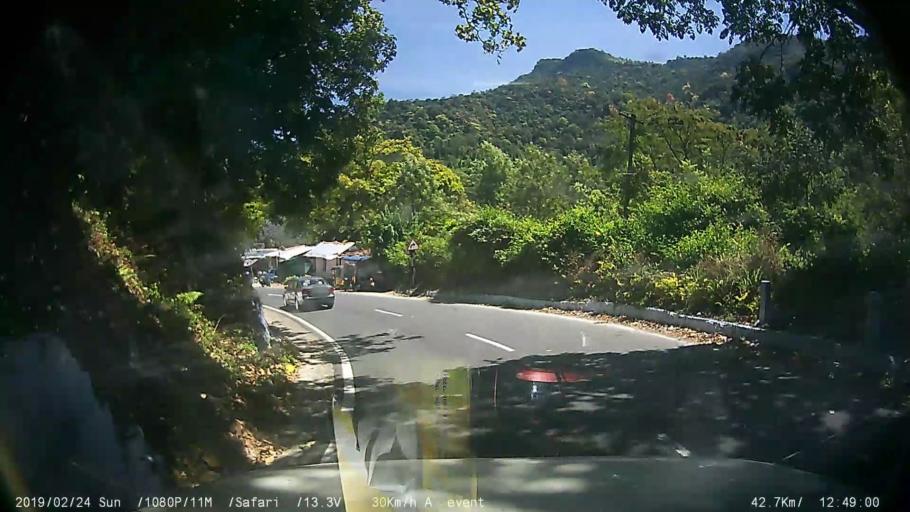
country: IN
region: Tamil Nadu
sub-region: Nilgiri
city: Wellington
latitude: 11.3296
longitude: 76.8041
